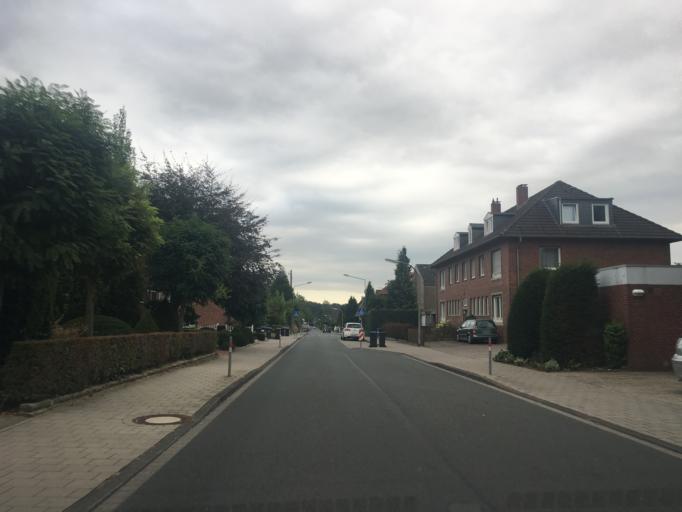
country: DE
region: North Rhine-Westphalia
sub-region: Regierungsbezirk Munster
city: Muenster
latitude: 51.9536
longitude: 7.5360
